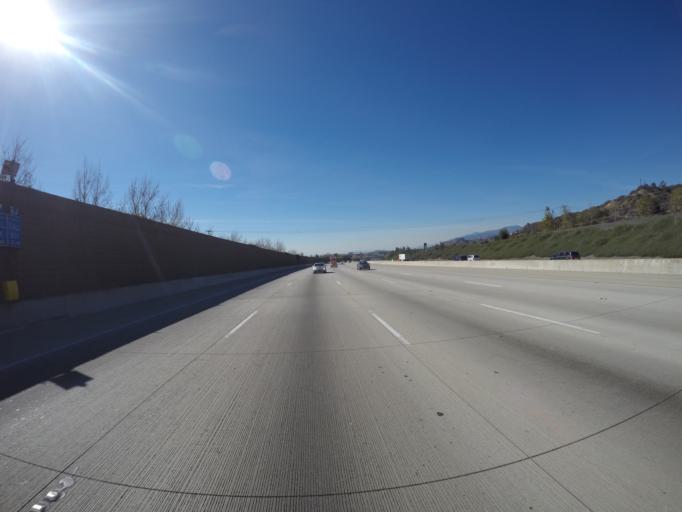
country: US
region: California
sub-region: Los Angeles County
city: La Verne
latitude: 34.1201
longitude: -117.7471
